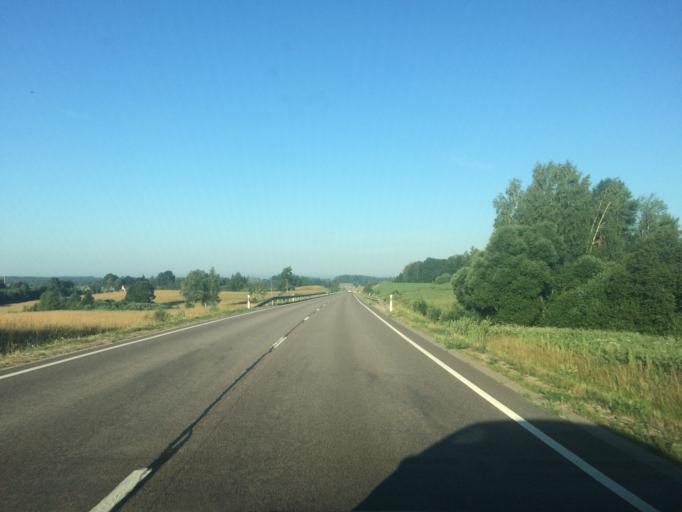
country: LT
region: Utenos apskritis
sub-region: Anyksciai
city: Anyksciai
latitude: 55.4193
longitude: 25.2190
